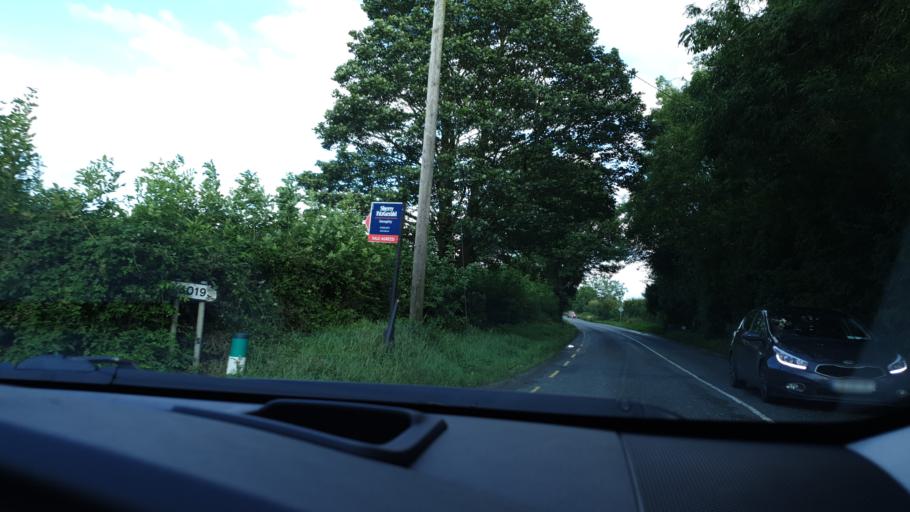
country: IE
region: Leinster
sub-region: An Mhi
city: Ashbourne
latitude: 53.4953
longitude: -6.3915
